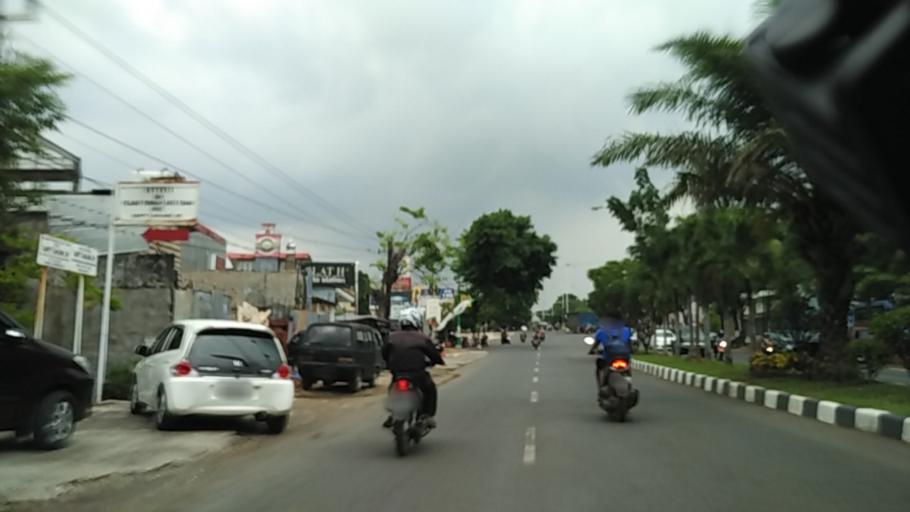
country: ID
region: Central Java
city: Semarang
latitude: -6.9885
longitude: 110.3933
